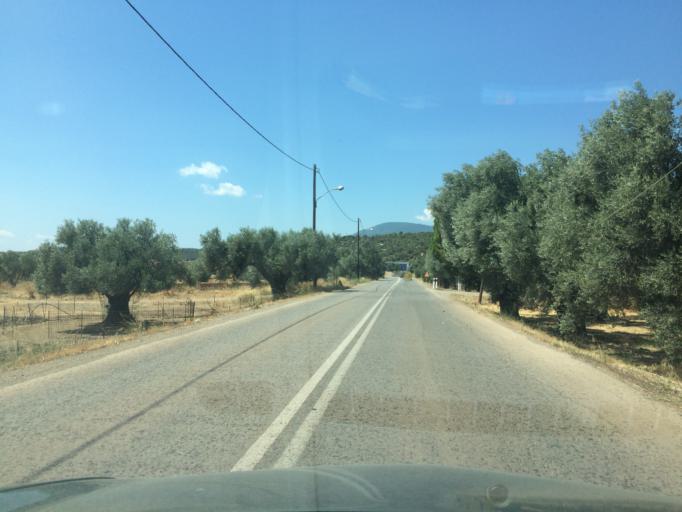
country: GR
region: Central Greece
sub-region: Nomos Evvoias
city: Psachna
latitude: 38.5801
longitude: 23.6244
